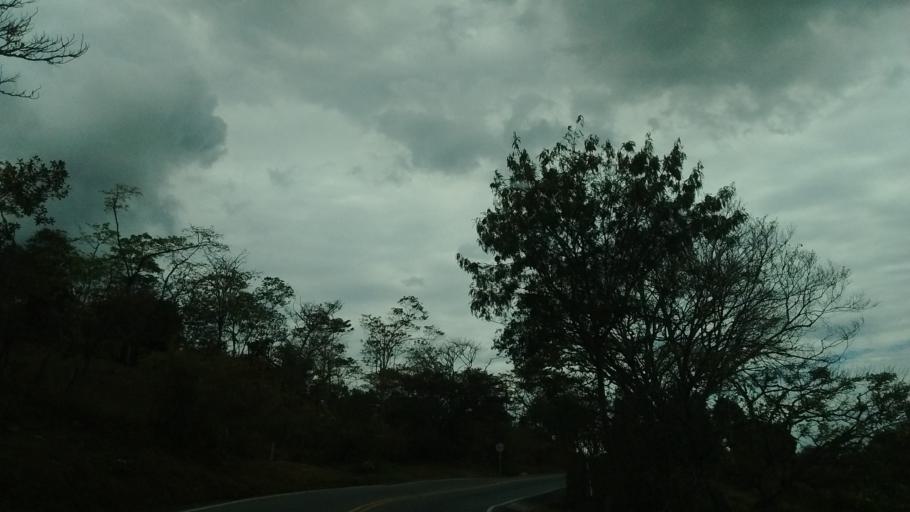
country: CO
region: Cauca
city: Rosas
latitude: 2.2743
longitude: -76.7201
